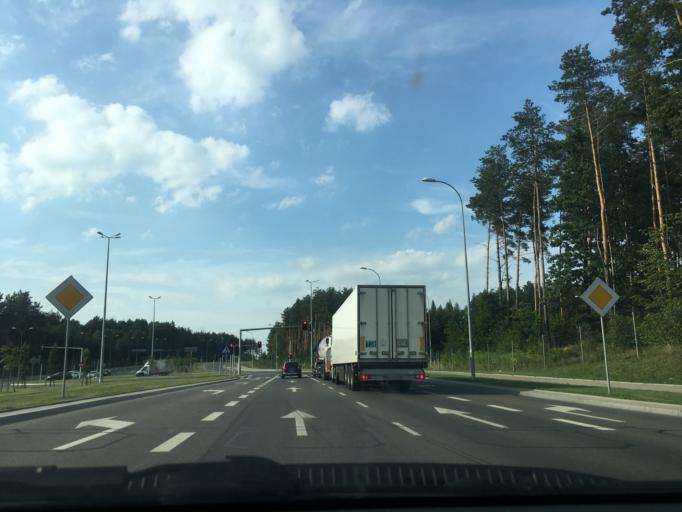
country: PL
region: Podlasie
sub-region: Bialystok
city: Bialystok
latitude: 53.1282
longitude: 23.2240
